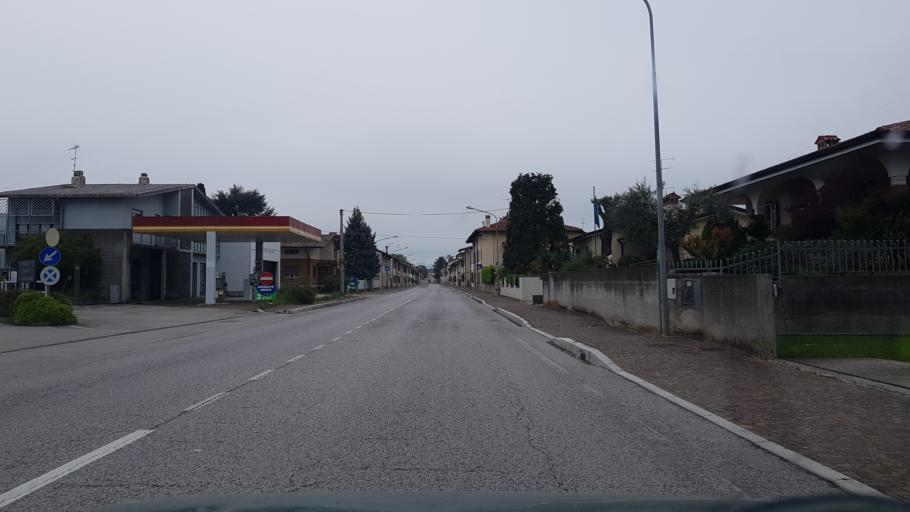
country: IT
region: Friuli Venezia Giulia
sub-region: Provincia di Gorizia
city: Mariano del Friuli
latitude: 45.9091
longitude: 13.4618
